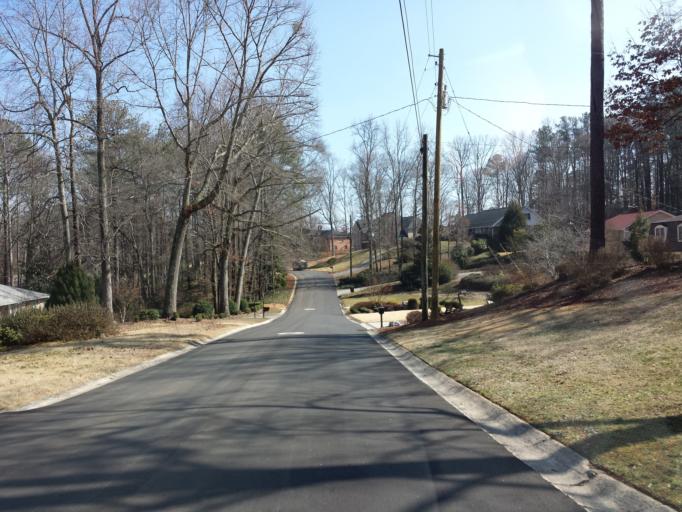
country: US
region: Georgia
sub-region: Cobb County
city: Vinings
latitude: 33.9203
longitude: -84.4605
